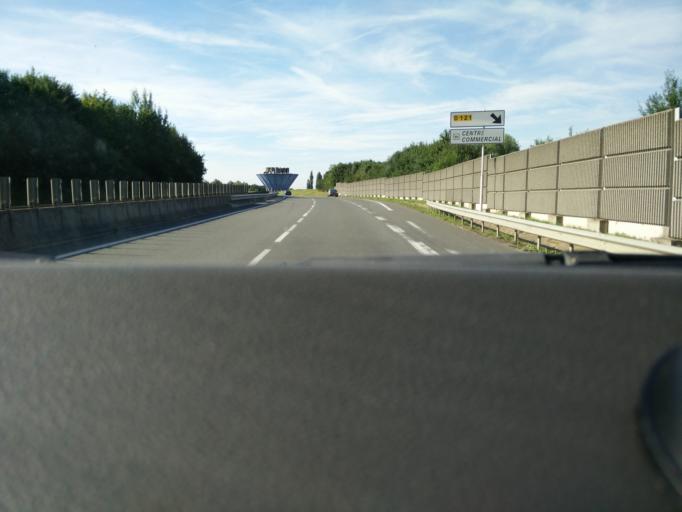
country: FR
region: Nord-Pas-de-Calais
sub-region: Departement du Nord
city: Hautmont
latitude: 50.2552
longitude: 3.9418
